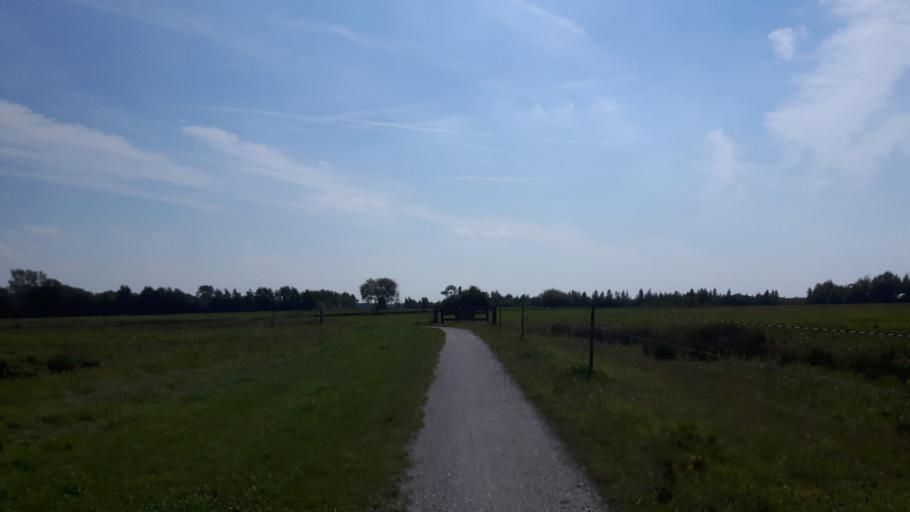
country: NL
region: Groningen
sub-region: Gemeente Hoogezand-Sappemeer
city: Hoogezand
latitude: 53.1362
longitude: 6.7194
